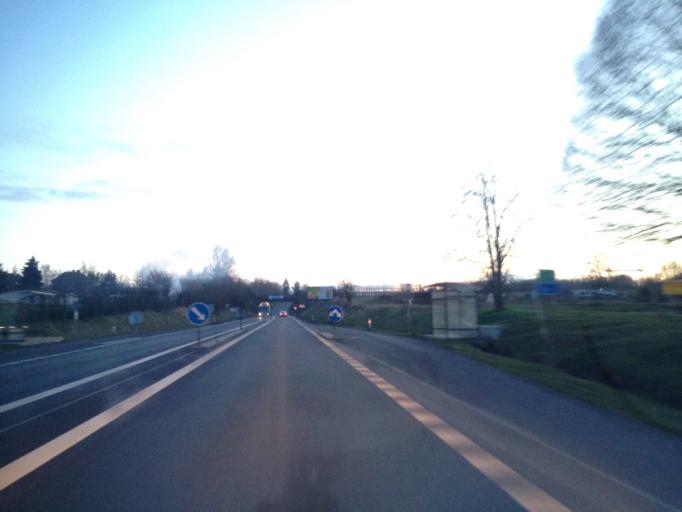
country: CZ
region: Ustecky
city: Kryry
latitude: 50.1391
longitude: 13.4367
